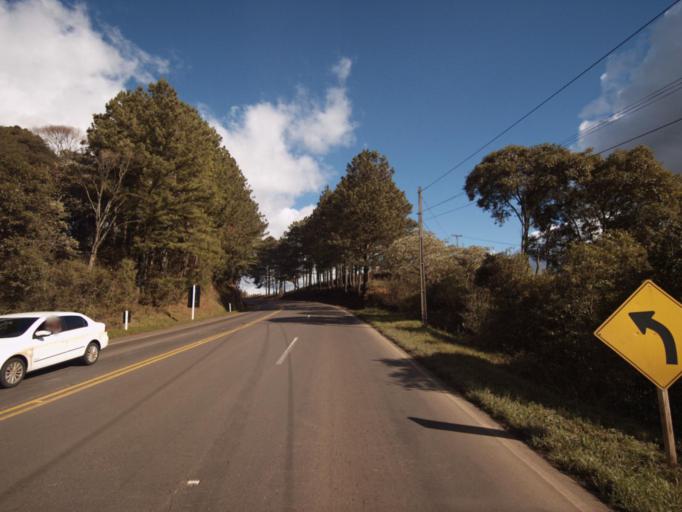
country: BR
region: Santa Catarina
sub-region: Joacaba
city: Joacaba
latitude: -27.0112
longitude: -51.7363
